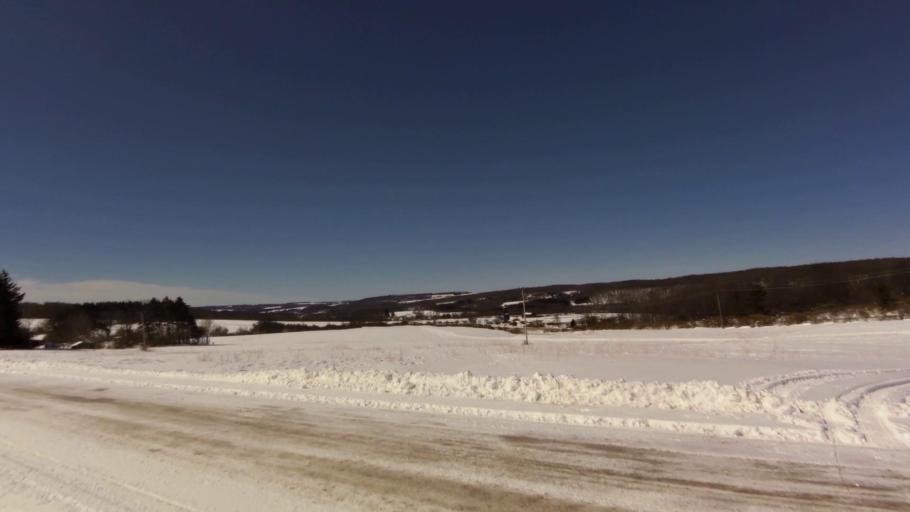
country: US
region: New York
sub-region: Wyoming County
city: Arcade
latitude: 42.4356
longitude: -78.3093
